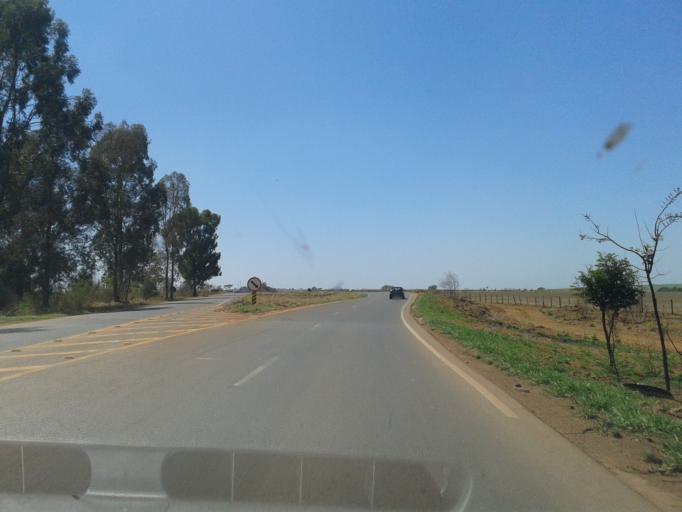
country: BR
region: Minas Gerais
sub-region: Araxa
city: Araxa
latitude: -19.4176
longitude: -47.2920
